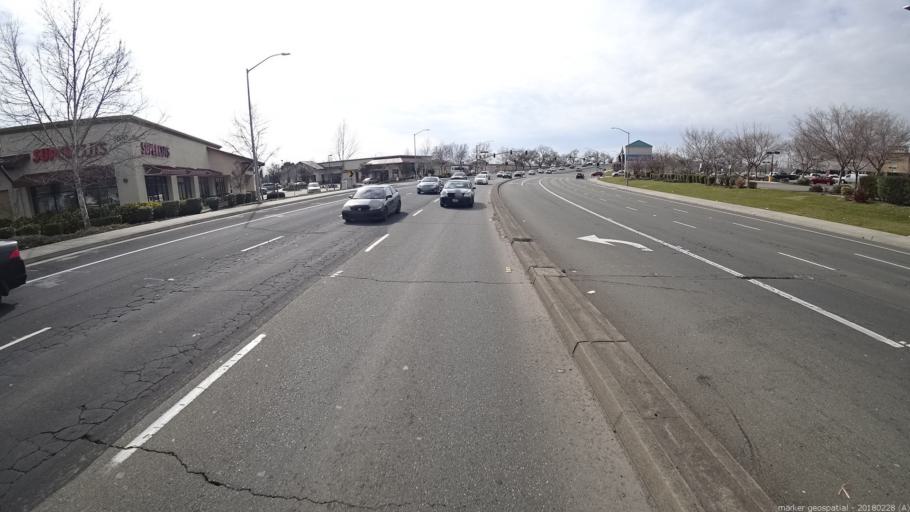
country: US
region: California
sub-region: Sacramento County
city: Antelope
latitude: 38.7026
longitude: -121.3305
